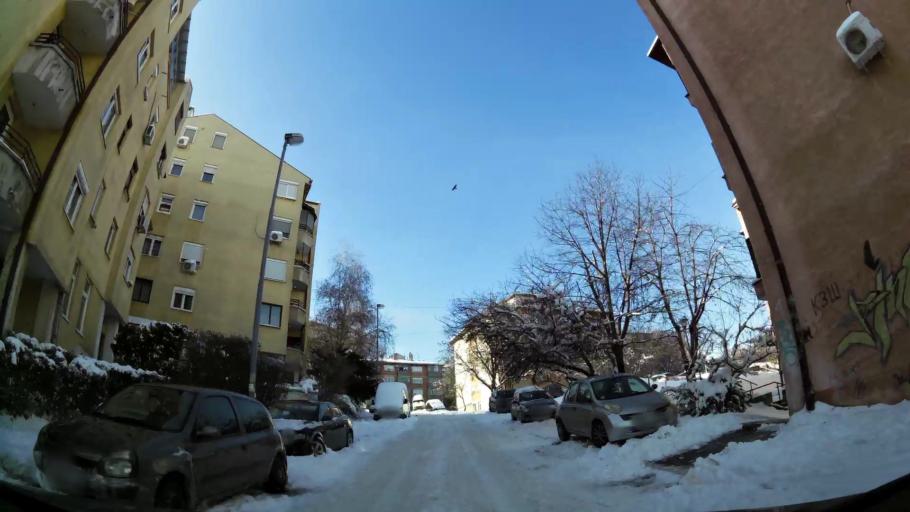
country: RS
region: Central Serbia
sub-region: Belgrade
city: Palilula
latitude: 44.8020
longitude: 20.5243
